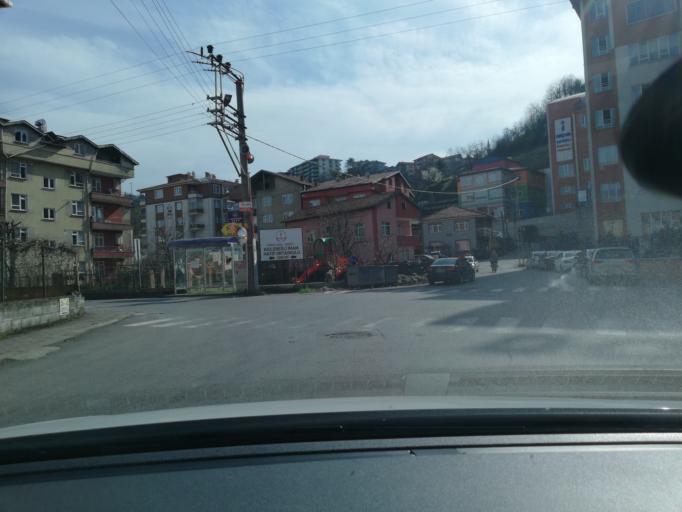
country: TR
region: Zonguldak
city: Eregli
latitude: 41.2687
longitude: 31.4479
